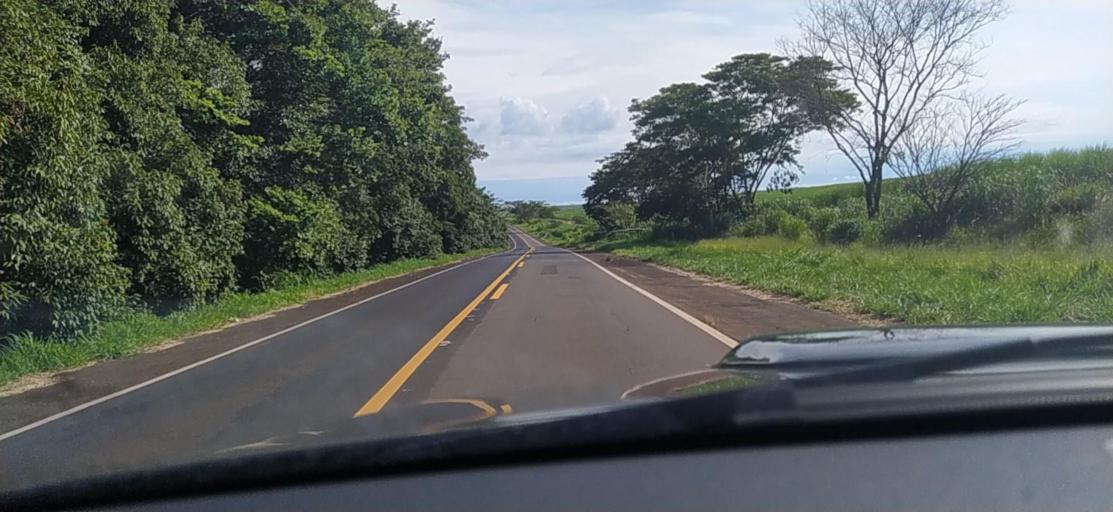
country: BR
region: Sao Paulo
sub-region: Catanduva
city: Catanduva
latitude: -21.0781
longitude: -49.0694
